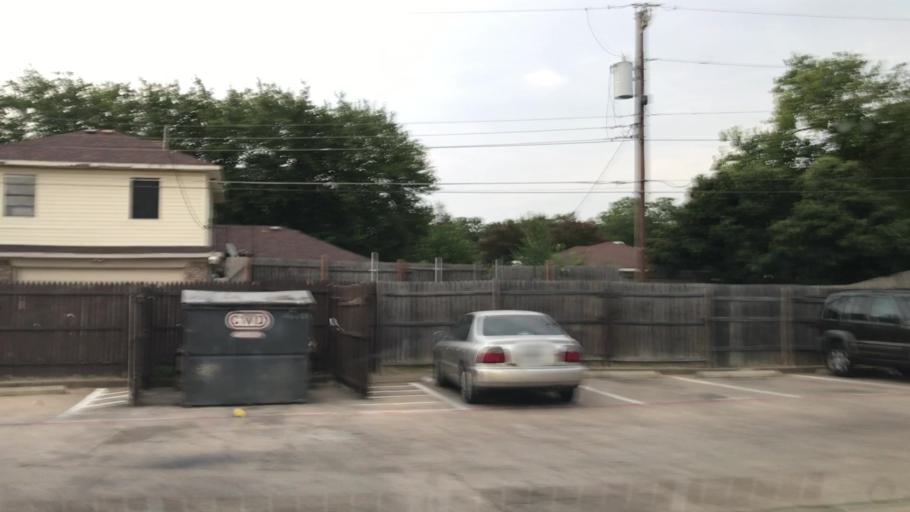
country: US
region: Texas
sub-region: Dallas County
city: Highland Park
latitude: 32.7910
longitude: -96.7106
